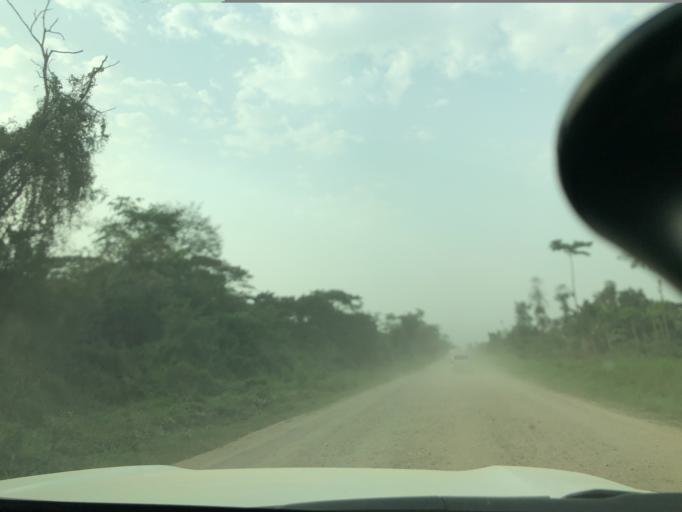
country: UG
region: Western Region
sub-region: Kasese District
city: Margherita
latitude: 0.2633
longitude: 29.6772
